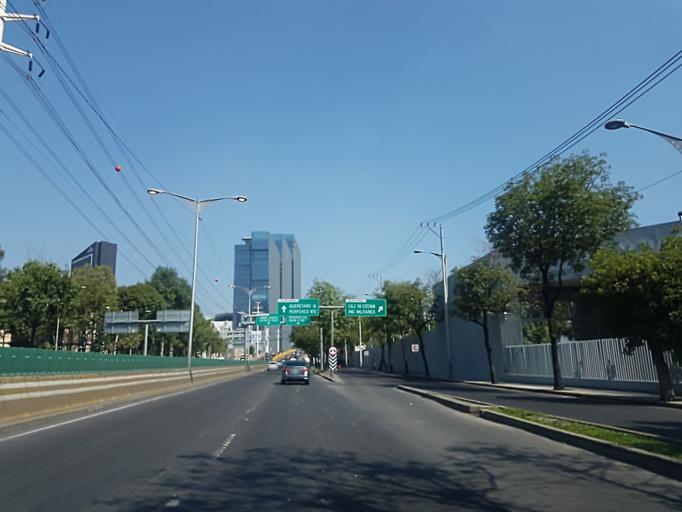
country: MX
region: Mexico City
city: Miguel Hidalgo
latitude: 19.4520
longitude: -99.2143
